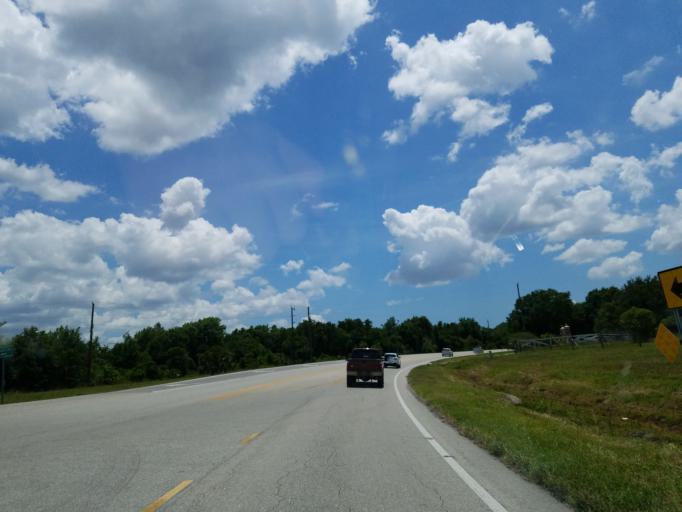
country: US
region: Florida
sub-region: Charlotte County
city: Harbour Heights
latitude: 27.0950
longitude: -82.0000
